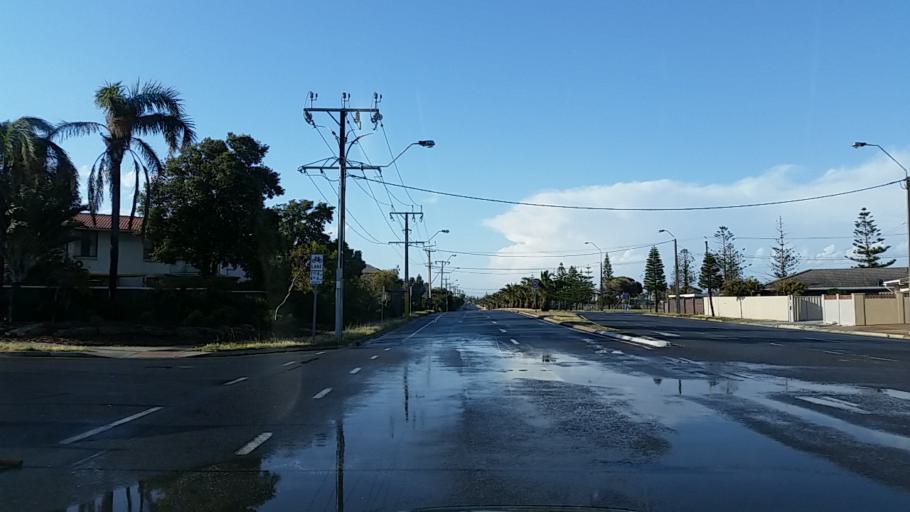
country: AU
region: South Australia
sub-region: Charles Sturt
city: West Lakes Shore
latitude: -34.8650
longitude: 138.4797
